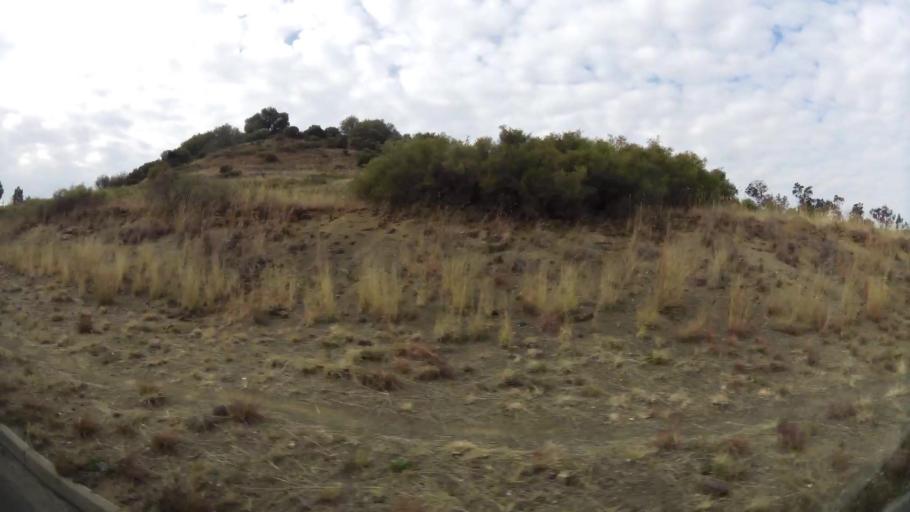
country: ZA
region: Orange Free State
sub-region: Mangaung Metropolitan Municipality
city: Bloemfontein
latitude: -29.1021
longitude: 26.2123
